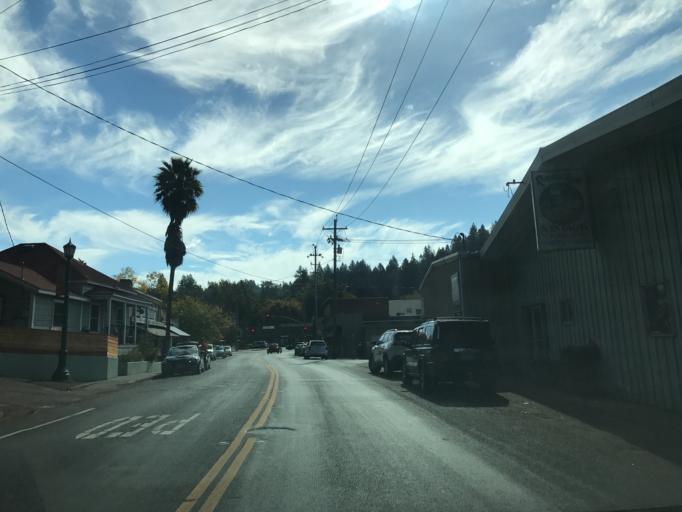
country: US
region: California
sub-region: Sonoma County
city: Guerneville
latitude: 38.5031
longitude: -122.9977
